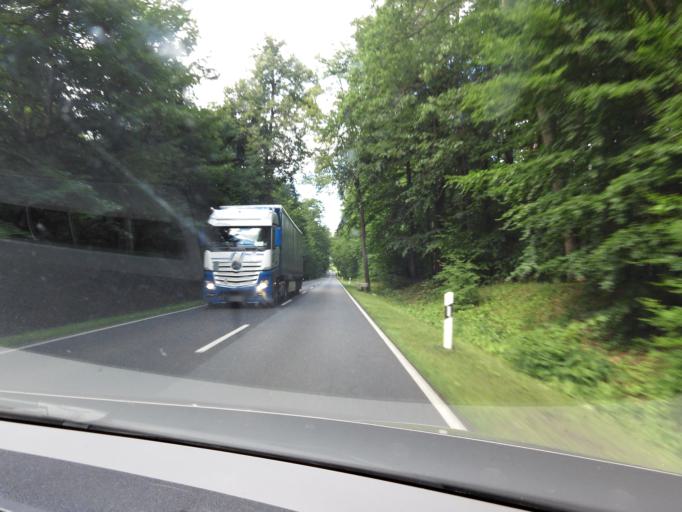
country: DE
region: Brandenburg
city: Furstenberg
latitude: 53.1328
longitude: 13.1600
